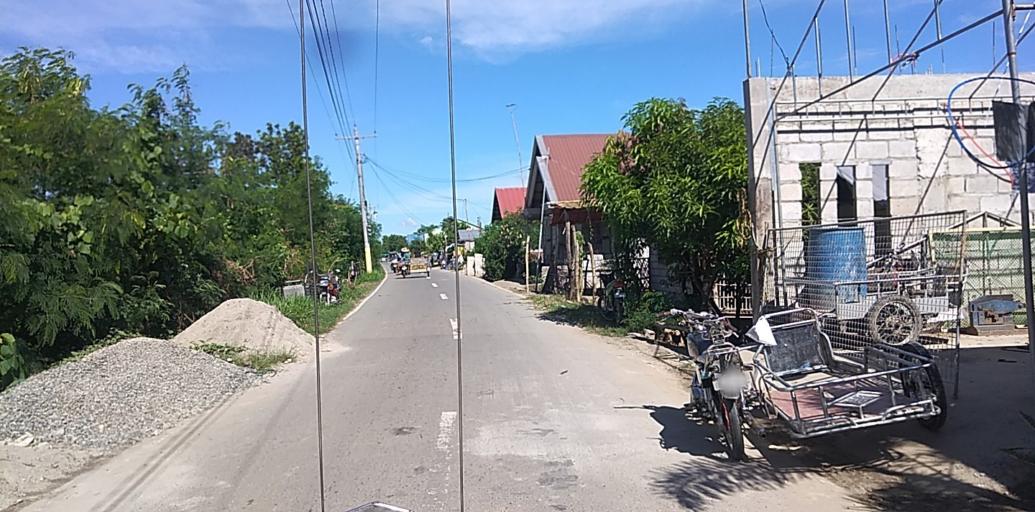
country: PH
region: Central Luzon
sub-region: Province of Pampanga
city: Candaba
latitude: 15.1101
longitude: 120.8166
